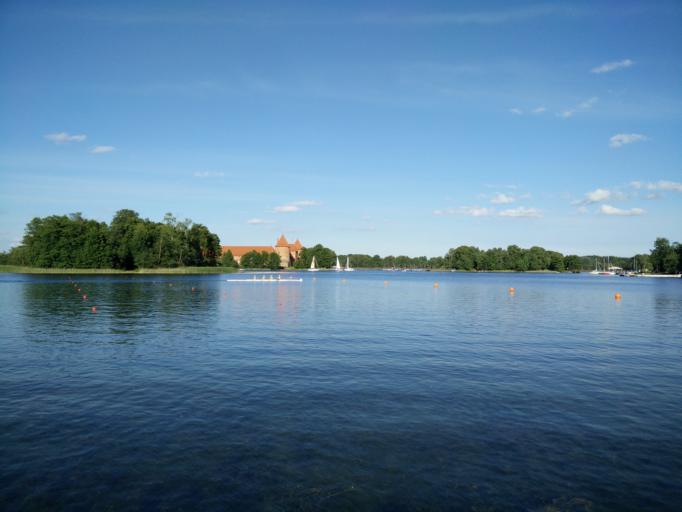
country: LT
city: Trakai
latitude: 54.6518
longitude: 24.9255
